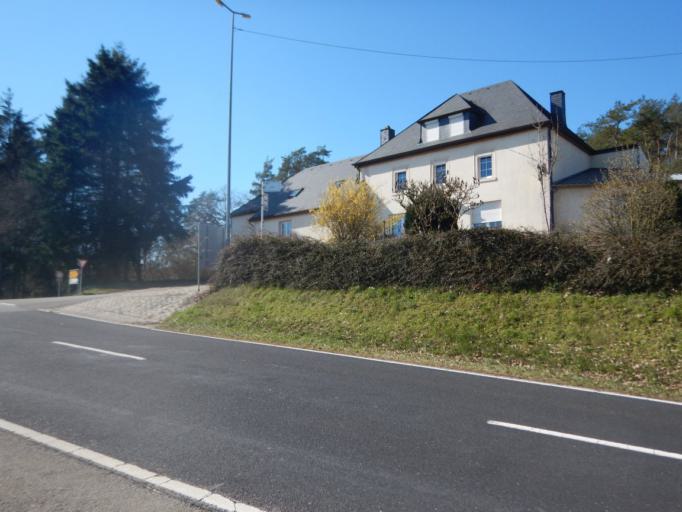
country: LU
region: Diekirch
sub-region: Canton de Wiltz
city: Eschweiler
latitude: 49.9859
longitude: 5.9597
